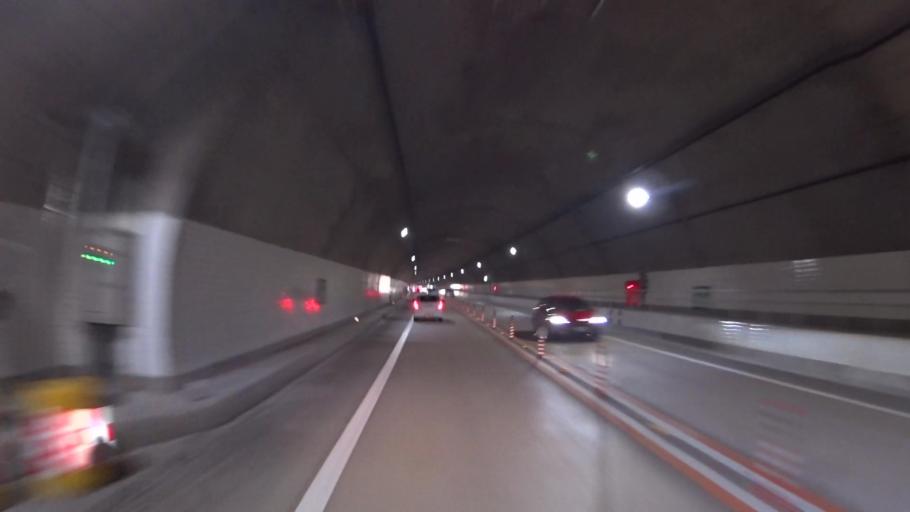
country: JP
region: Kyoto
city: Ayabe
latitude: 35.2396
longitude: 135.3441
